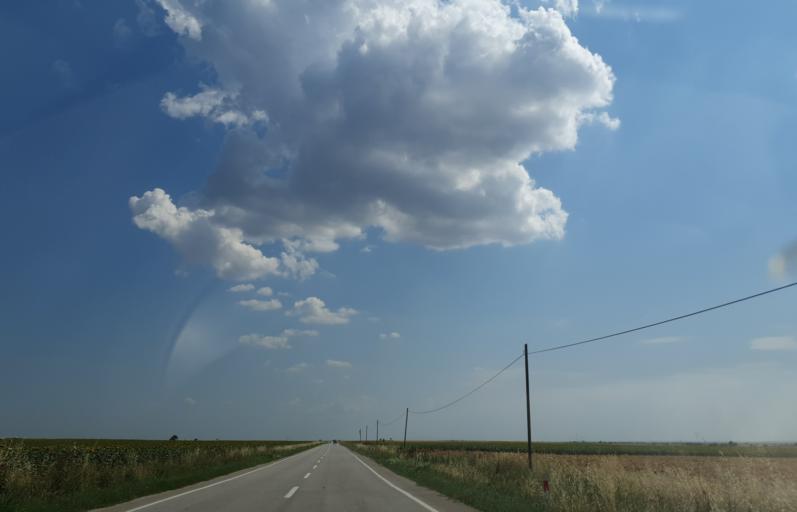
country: TR
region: Kirklareli
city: Buyukkaristiran
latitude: 41.4203
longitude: 27.5796
